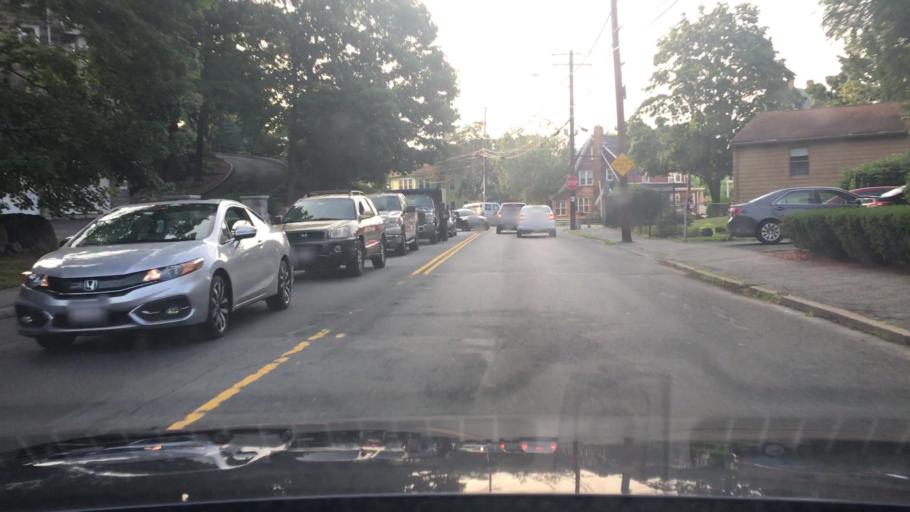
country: US
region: Massachusetts
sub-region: Essex County
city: Lynn
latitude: 42.4699
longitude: -70.9756
